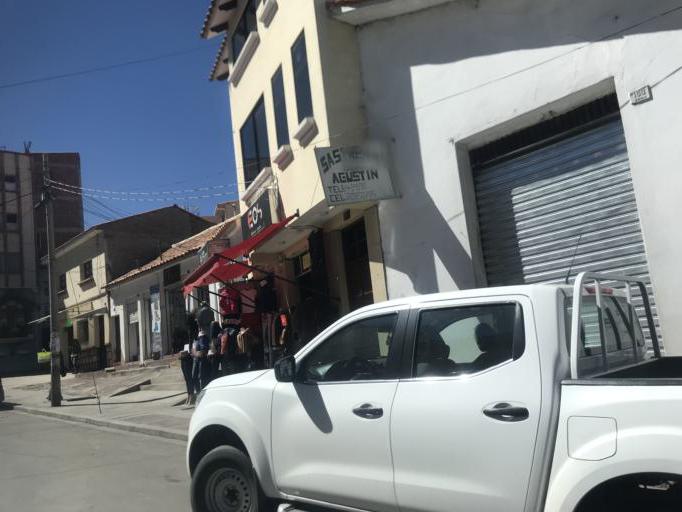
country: BO
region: Chuquisaca
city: Sucre
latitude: -19.0421
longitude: -65.2570
